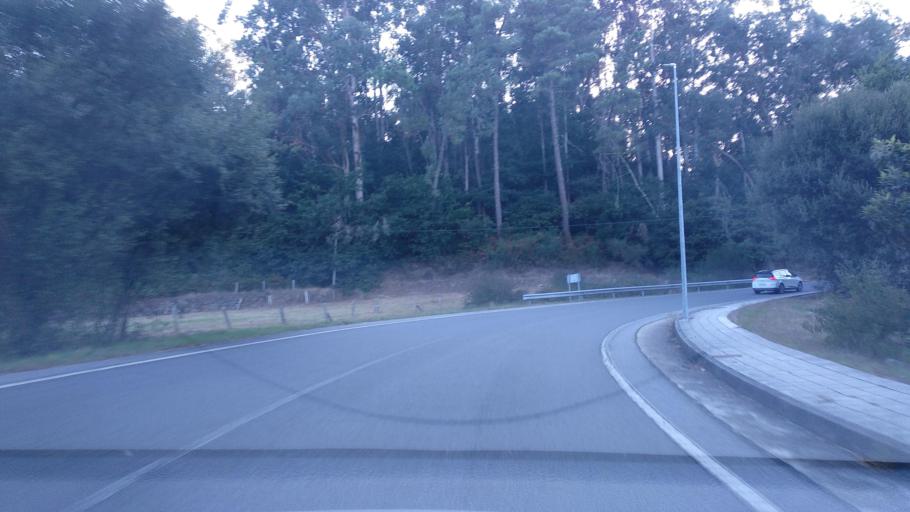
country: ES
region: Galicia
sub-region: Provincia de Pontevedra
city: Redondela
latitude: 42.3340
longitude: -8.5806
